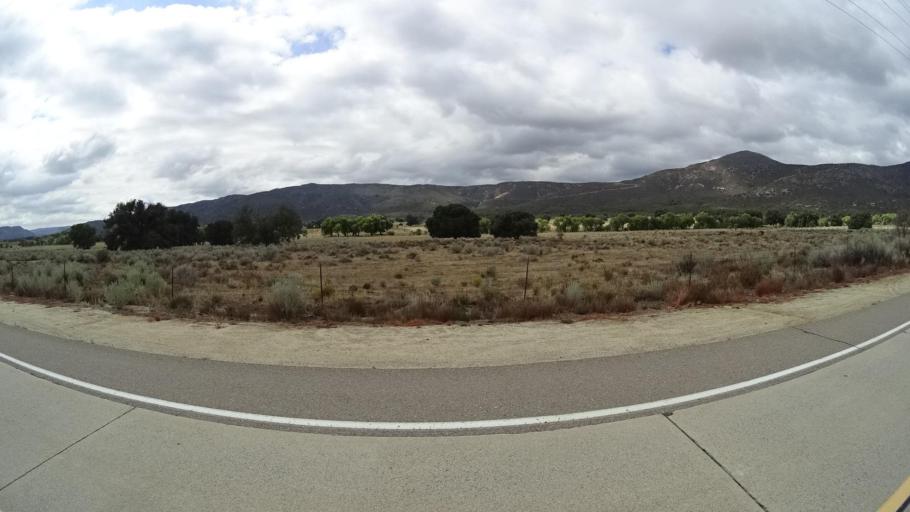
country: US
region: California
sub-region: San Diego County
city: Pine Valley
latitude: 32.7527
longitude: -116.4850
